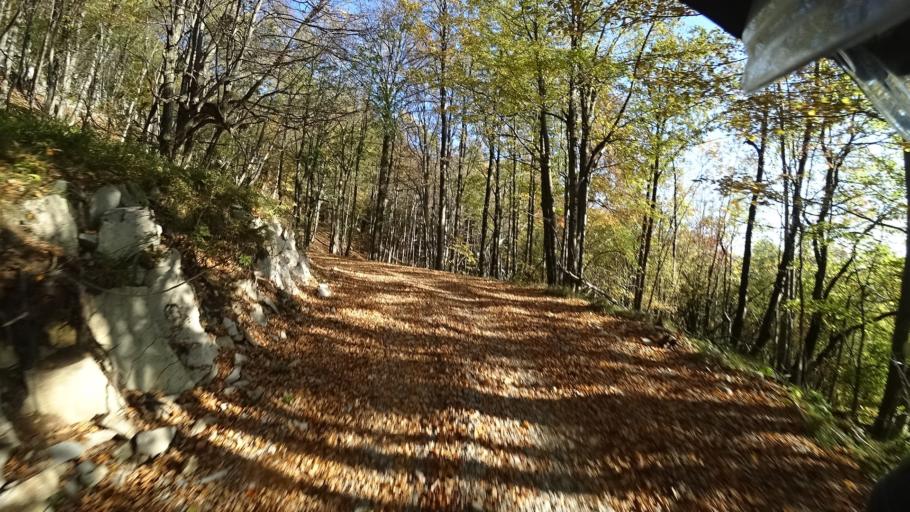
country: HR
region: Primorsko-Goranska
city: Klana
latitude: 45.4847
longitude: 14.4155
